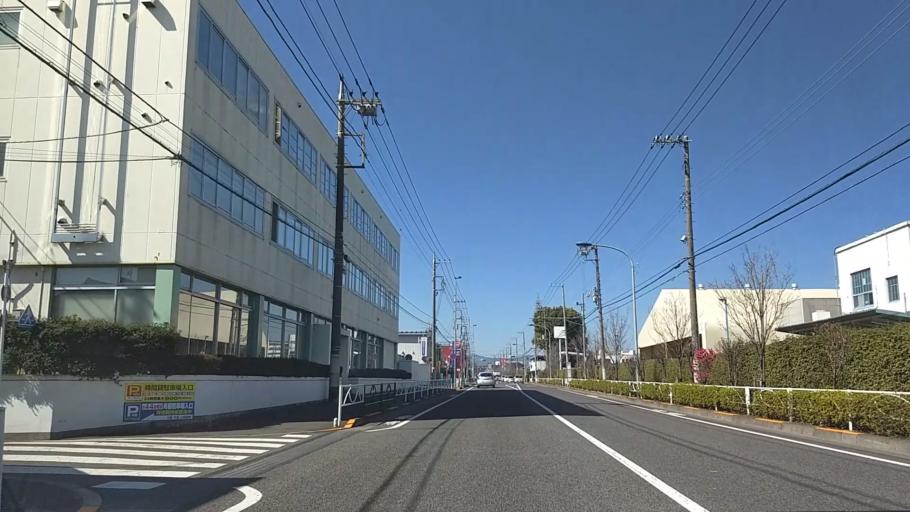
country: JP
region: Tokyo
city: Hino
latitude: 35.6724
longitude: 139.3808
